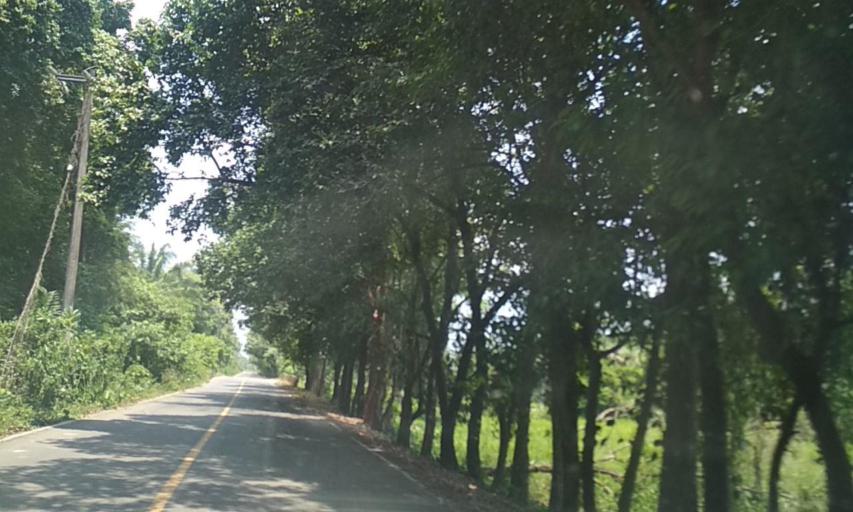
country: MX
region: Tabasco
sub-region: Huimanguillo
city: Francisco Rueda
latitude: 17.7564
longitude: -94.0271
